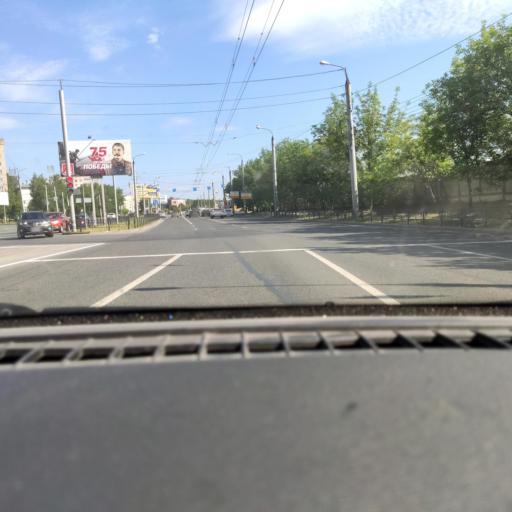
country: RU
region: Udmurtiya
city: Izhevsk
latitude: 56.8842
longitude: 53.2587
